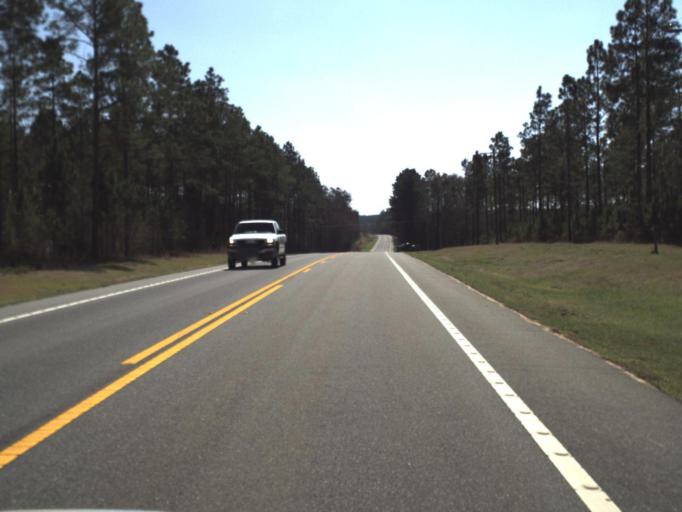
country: US
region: Florida
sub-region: Jackson County
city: Sneads
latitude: 30.6169
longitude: -85.0296
